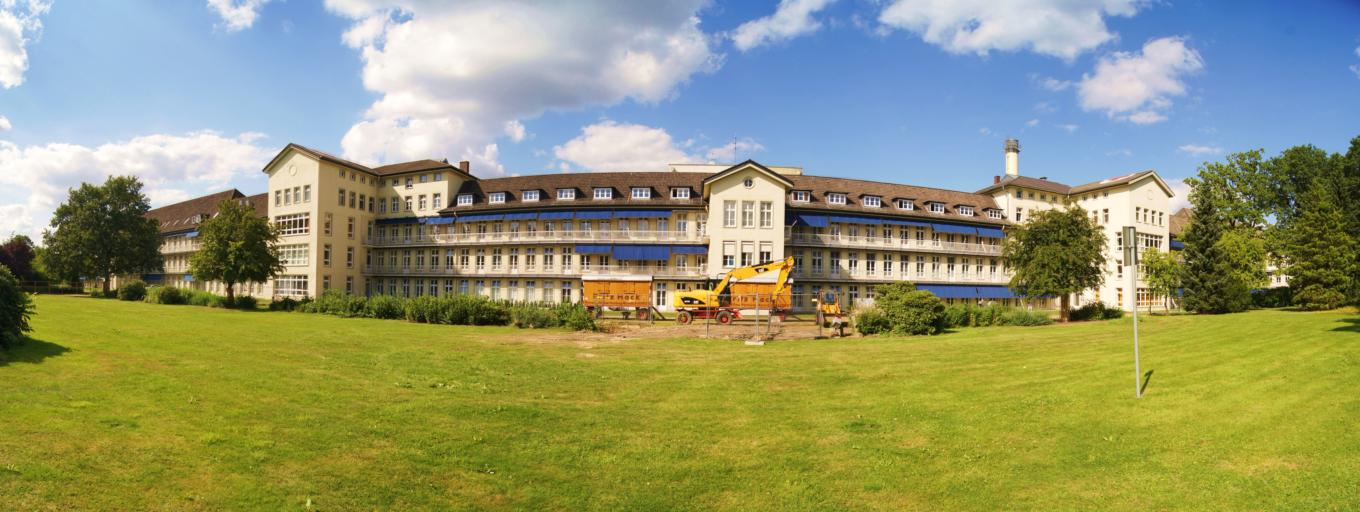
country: DE
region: Hamburg
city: Steilshoop
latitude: 53.5940
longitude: 10.0772
